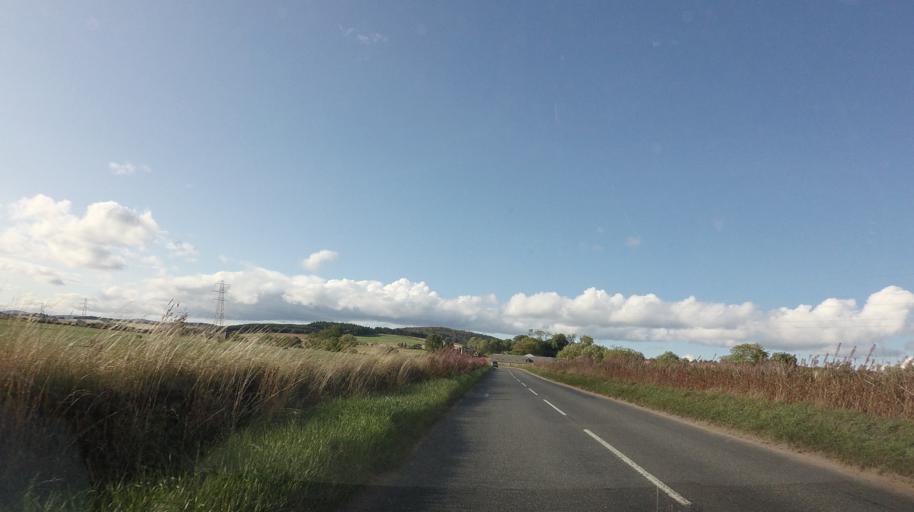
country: GB
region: Scotland
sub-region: Aberdeenshire
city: Banchory
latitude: 57.1338
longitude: -2.4283
